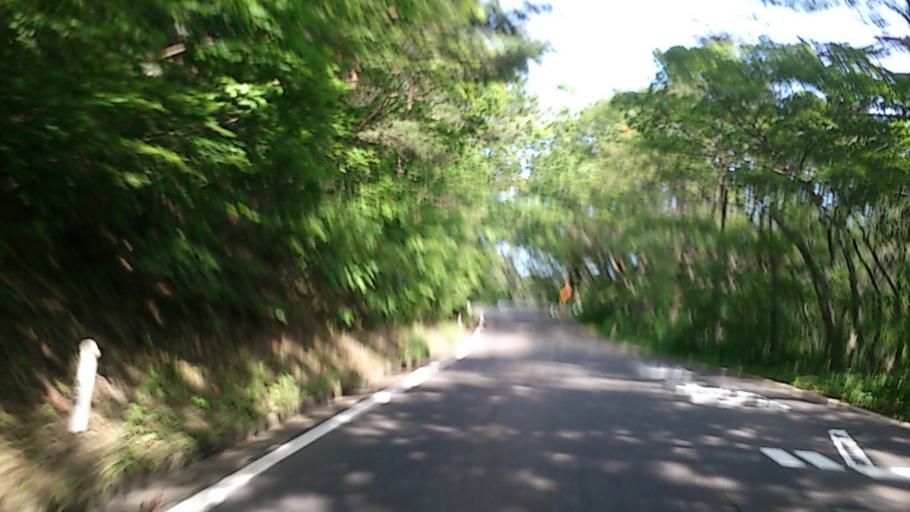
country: JP
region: Aomori
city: Aomori Shi
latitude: 40.7148
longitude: 140.8185
